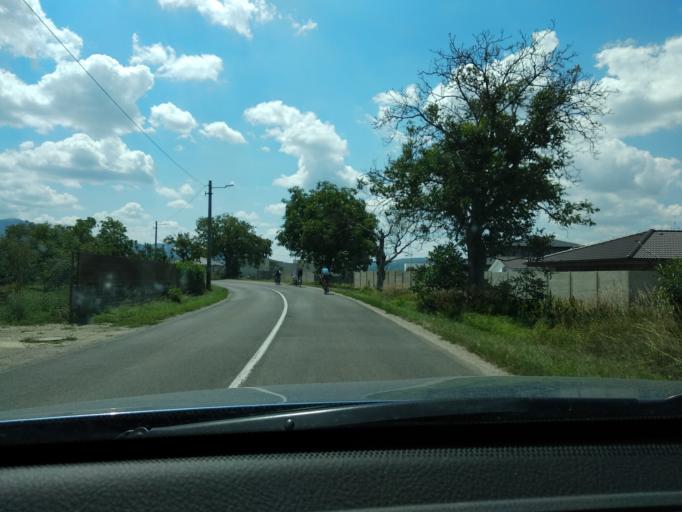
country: SK
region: Trenciansky
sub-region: Okres Trencin
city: Trencin
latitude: 48.8575
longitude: 18.0178
